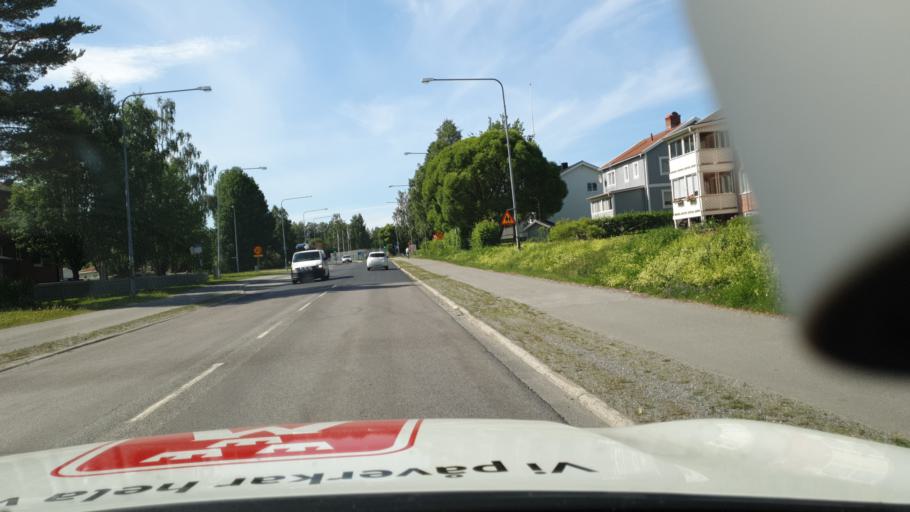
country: SE
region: Vaesterbotten
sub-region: Skelleftea Kommun
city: Viken
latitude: 64.7569
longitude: 20.9153
